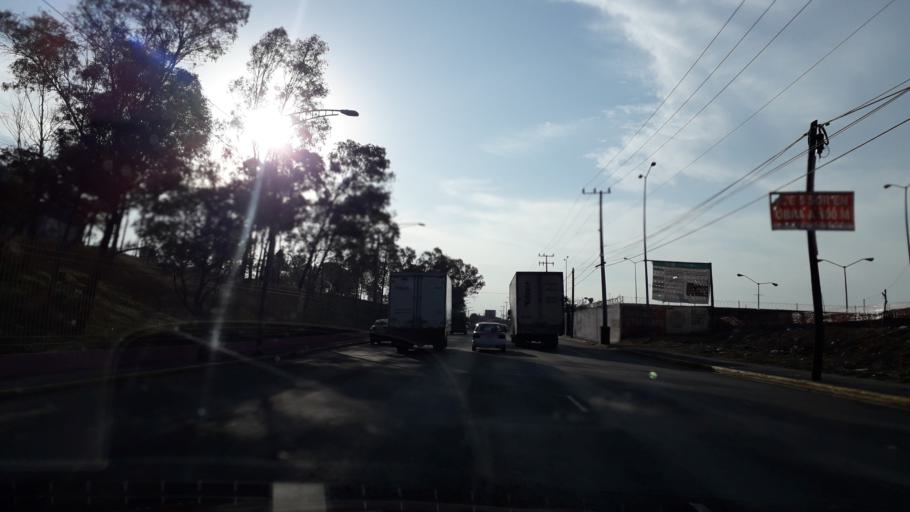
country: MX
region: Mexico City
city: Iztapalapa
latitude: 19.3676
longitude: -99.0429
